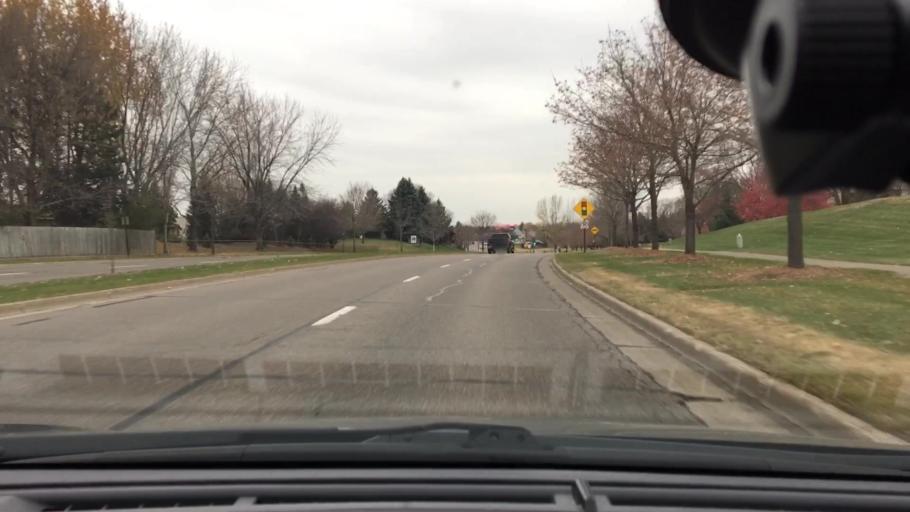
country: US
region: Minnesota
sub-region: Hennepin County
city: Maple Grove
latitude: 45.1100
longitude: -93.4513
